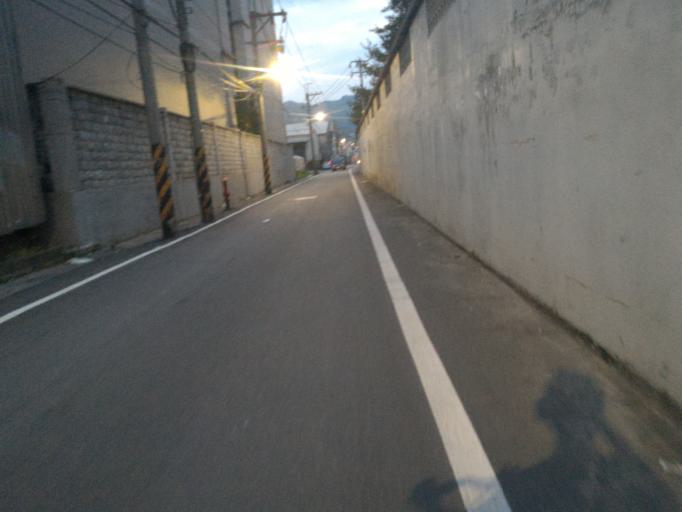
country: TW
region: Taiwan
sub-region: Taoyuan
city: Taoyuan
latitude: 24.9613
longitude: 121.3925
